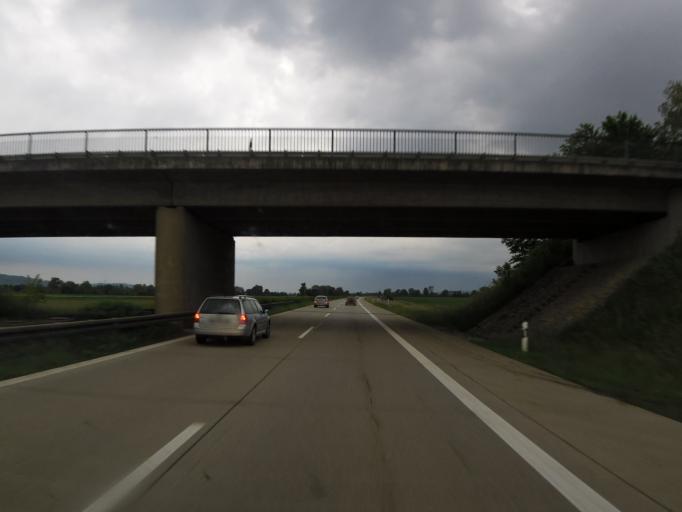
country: DE
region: Bavaria
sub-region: Lower Bavaria
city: Niederviehbach
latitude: 48.6370
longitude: 12.3759
